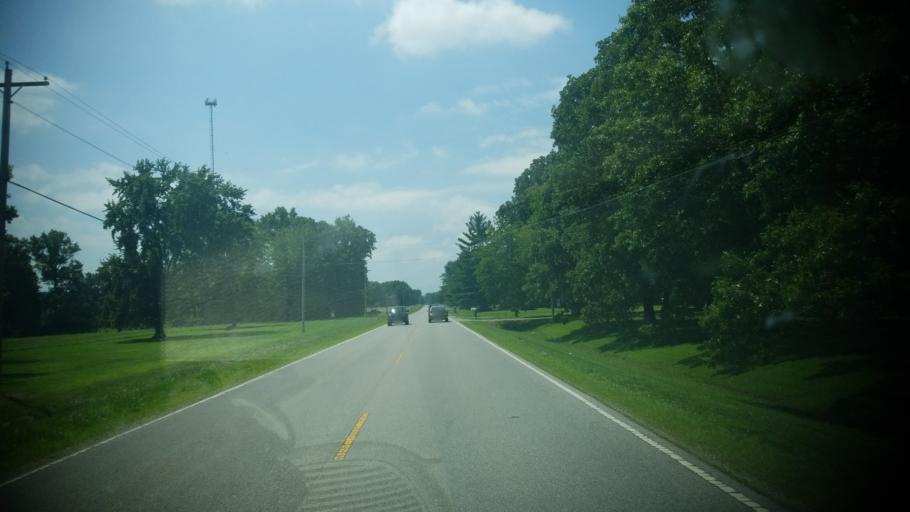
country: US
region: Illinois
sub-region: Wayne County
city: Fairfield
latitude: 38.3989
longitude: -88.3505
